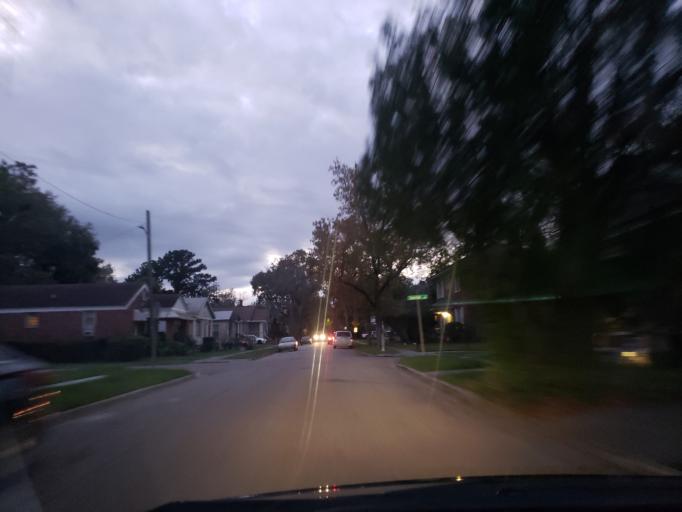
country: US
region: Georgia
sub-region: Chatham County
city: Thunderbolt
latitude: 32.0492
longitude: -81.0827
